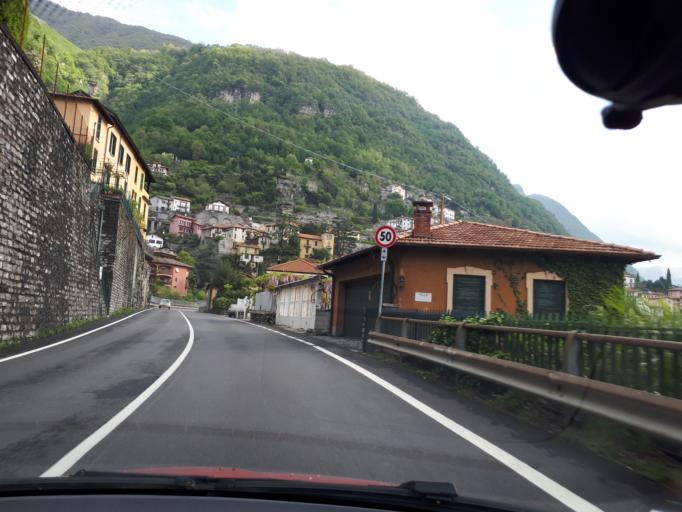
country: IT
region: Lombardy
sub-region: Provincia di Como
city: Moltrasio
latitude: 45.8613
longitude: 9.0980
